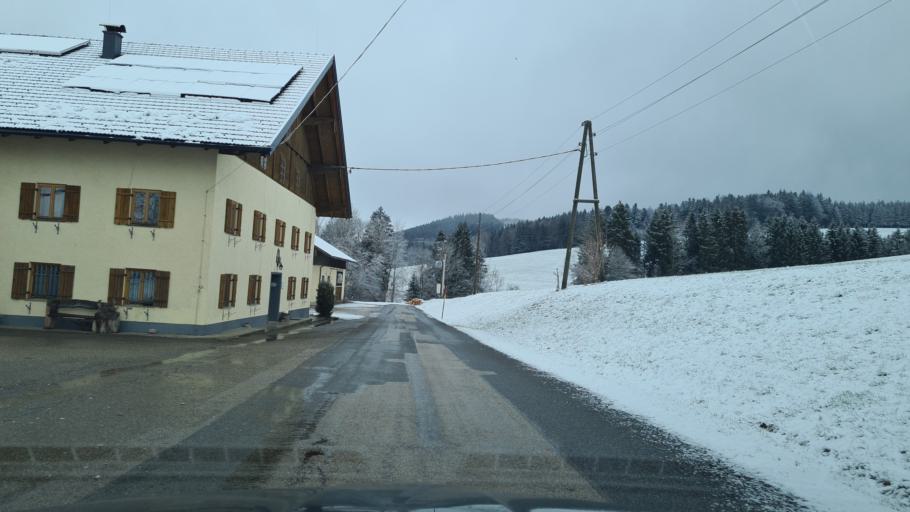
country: AT
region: Upper Austria
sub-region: Politischer Bezirk Vocklabruck
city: Oberhofen am Irrsee
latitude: 47.9383
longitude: 13.3224
